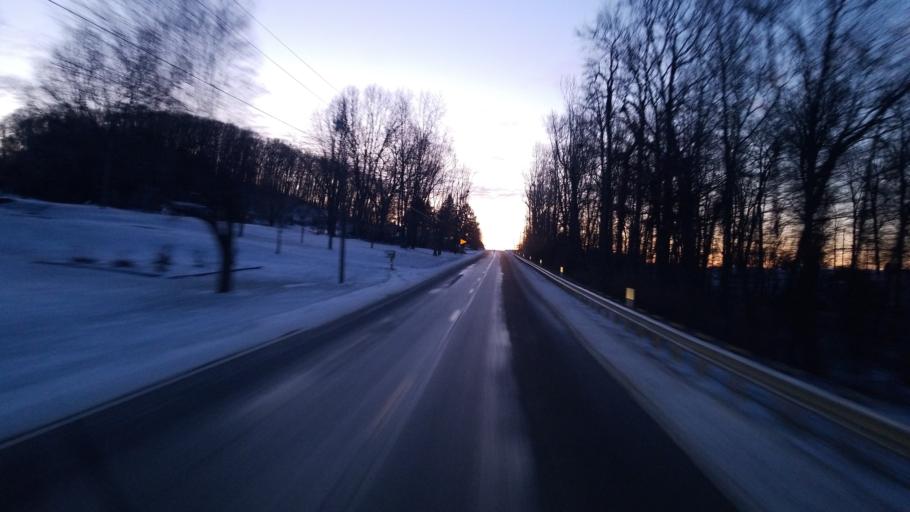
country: US
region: Pennsylvania
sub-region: Clarion County
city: Knox
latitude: 41.2643
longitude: -79.5611
